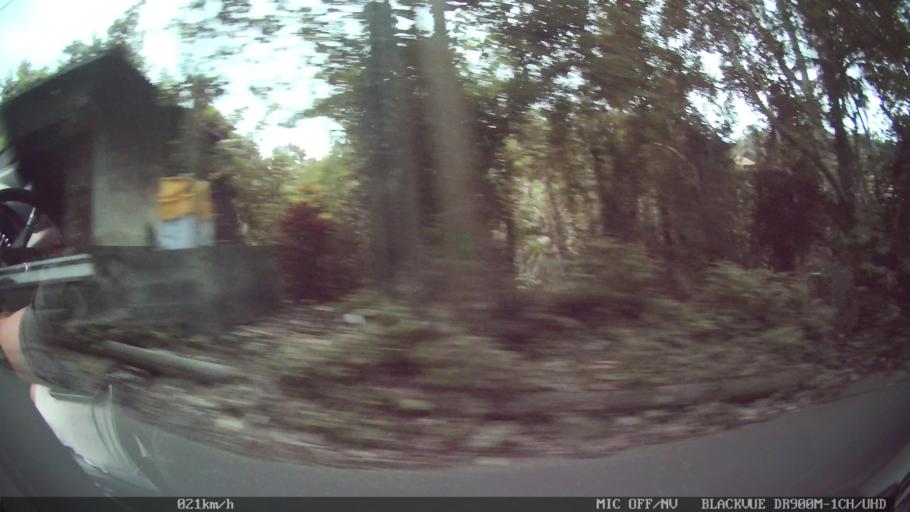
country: ID
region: Bali
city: Bunutan
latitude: -8.4797
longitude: 115.2552
